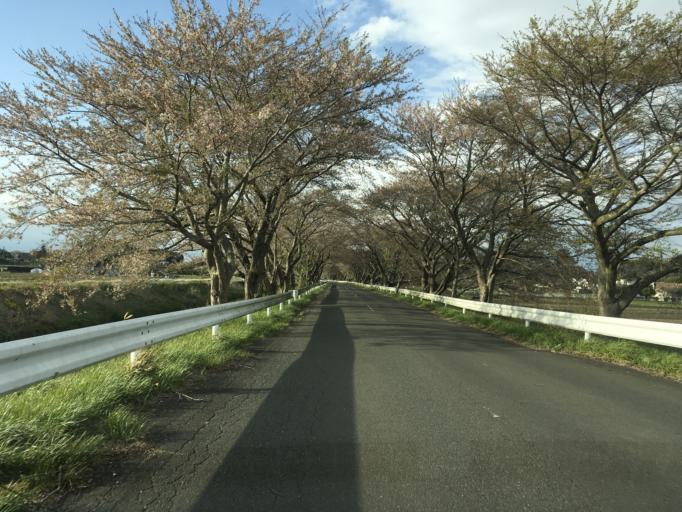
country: JP
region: Miyagi
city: Wakuya
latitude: 38.6532
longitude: 141.1461
